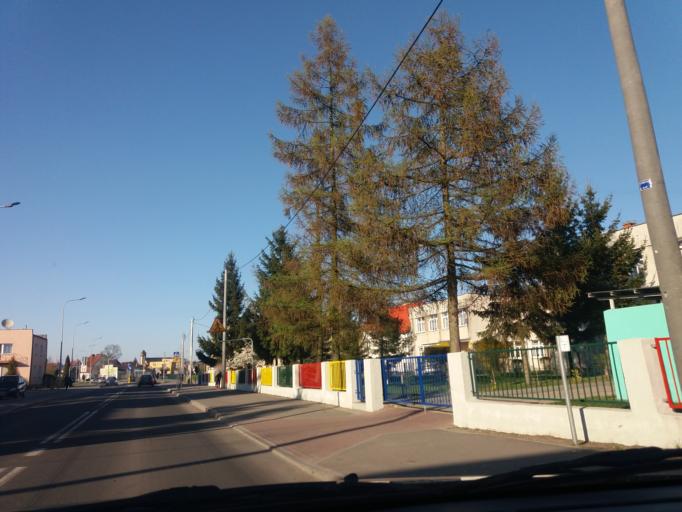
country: PL
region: Warmian-Masurian Voivodeship
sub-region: Powiat nidzicki
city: Nidzica
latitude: 53.3660
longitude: 20.4285
